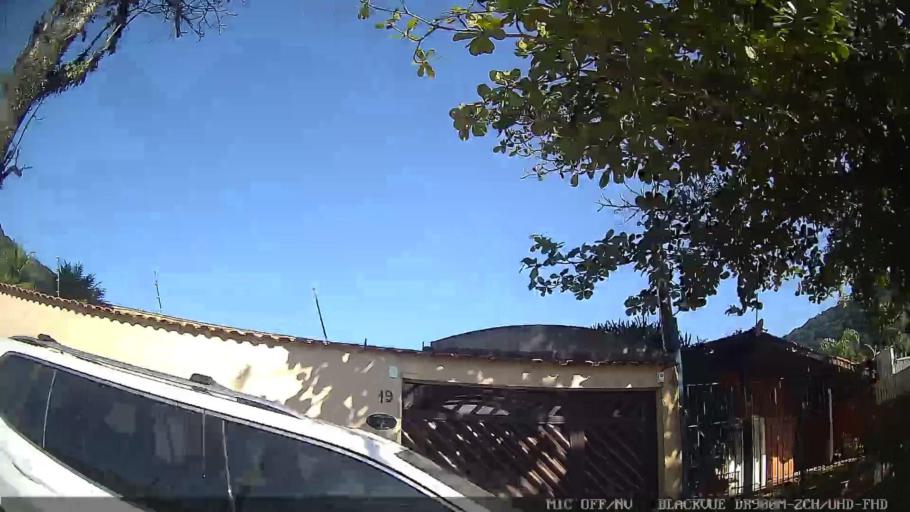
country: BR
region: Sao Paulo
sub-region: Guaruja
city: Guaruja
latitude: -24.0140
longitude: -46.2822
